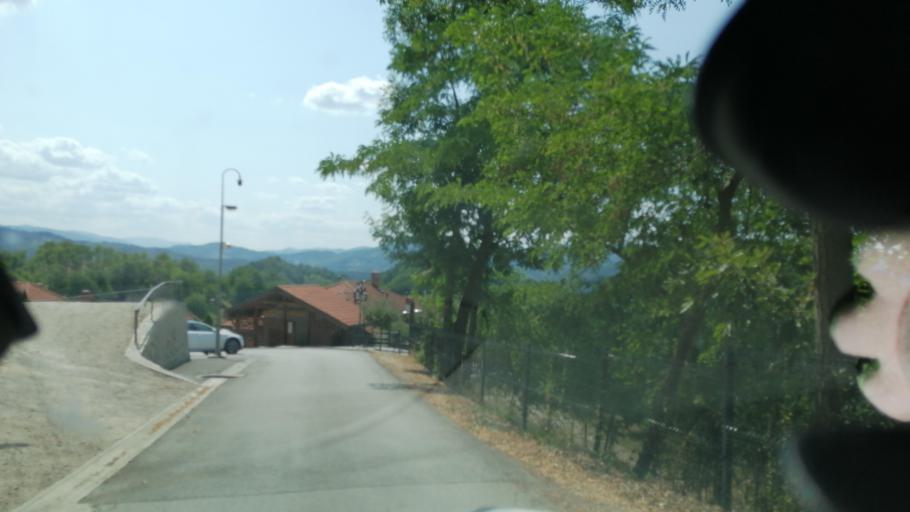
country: RS
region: Central Serbia
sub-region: Moravicki Okrug
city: Ivanjica
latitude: 43.6180
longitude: 20.2479
